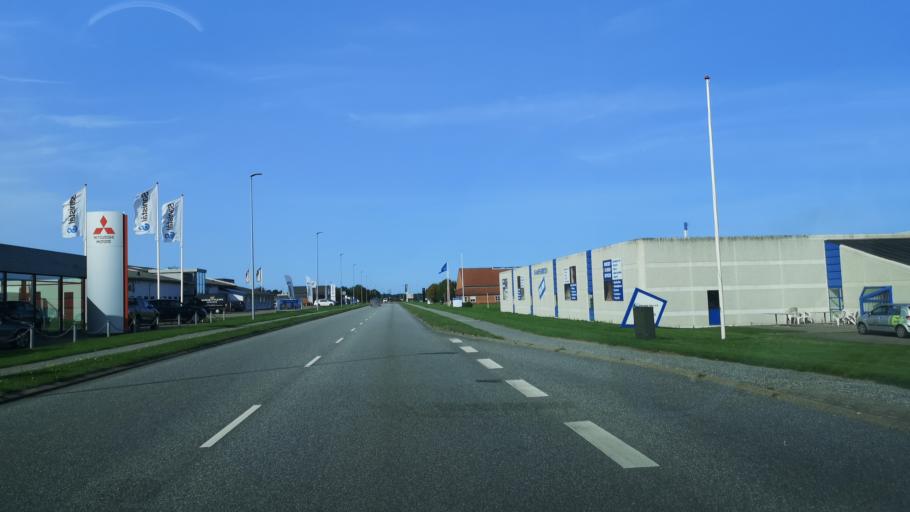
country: DK
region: Central Jutland
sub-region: Herning Kommune
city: Herning
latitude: 56.1561
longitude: 8.9758
